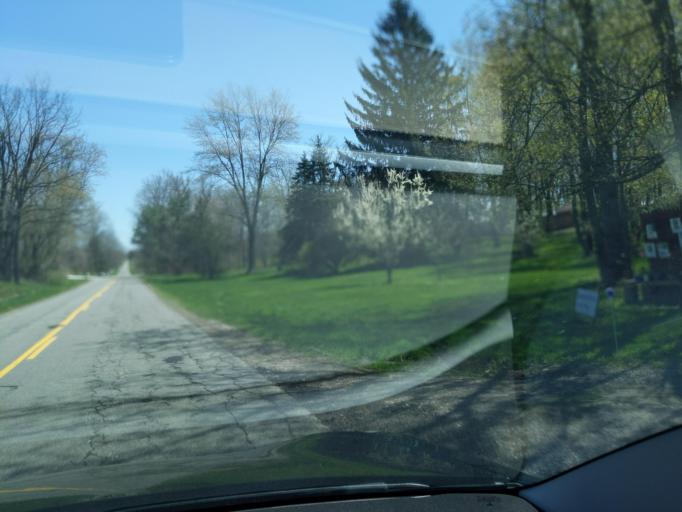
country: US
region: Michigan
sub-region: Ingham County
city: Holt
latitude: 42.5530
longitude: -84.5585
